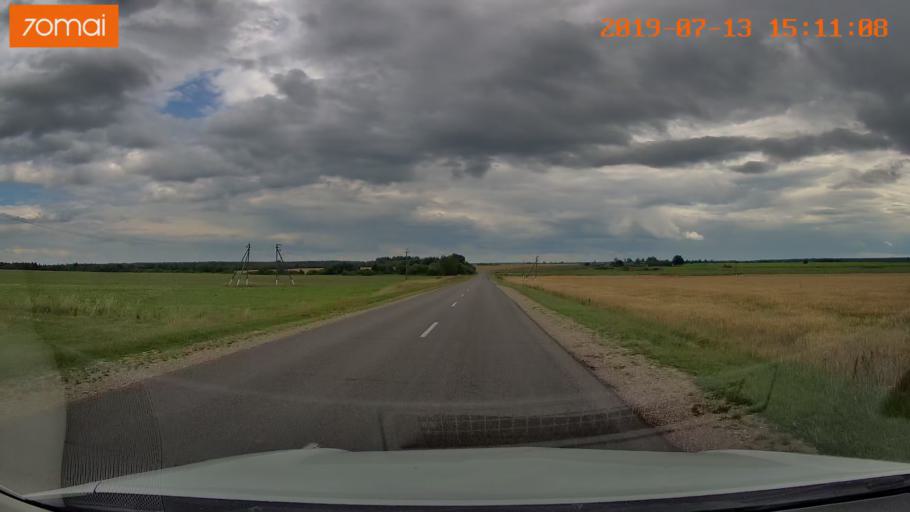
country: BY
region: Mogilev
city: Hlusha
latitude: 53.1649
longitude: 28.7821
